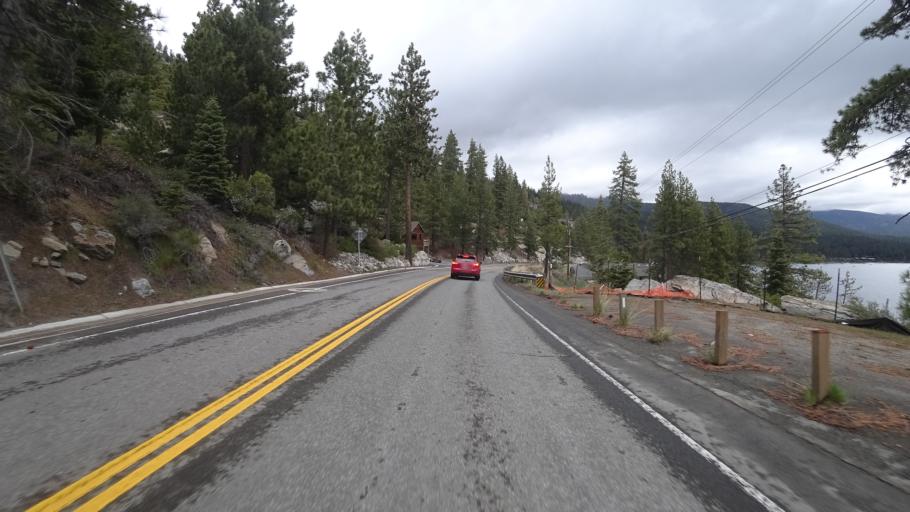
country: US
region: California
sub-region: Placer County
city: Kings Beach
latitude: 39.2415
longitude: -120.0006
